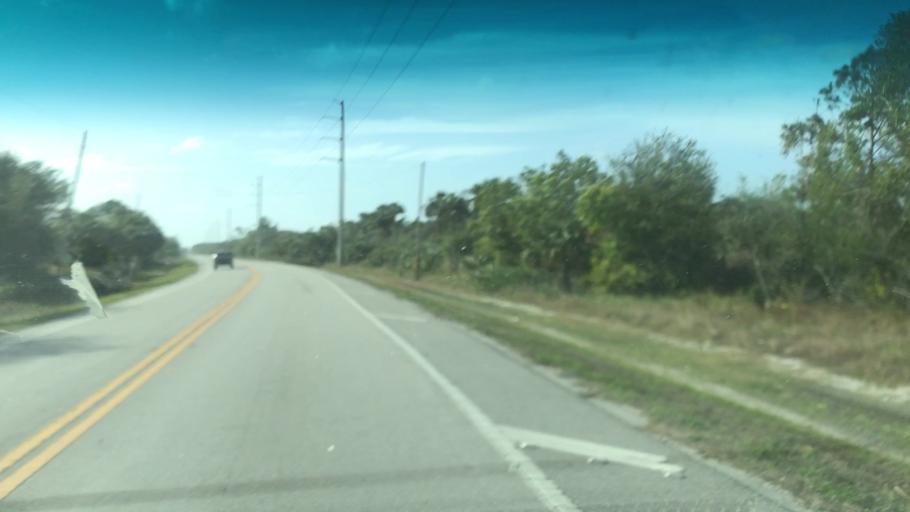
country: US
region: Florida
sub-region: Collier County
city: Orangetree
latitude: 26.3592
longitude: -81.5955
